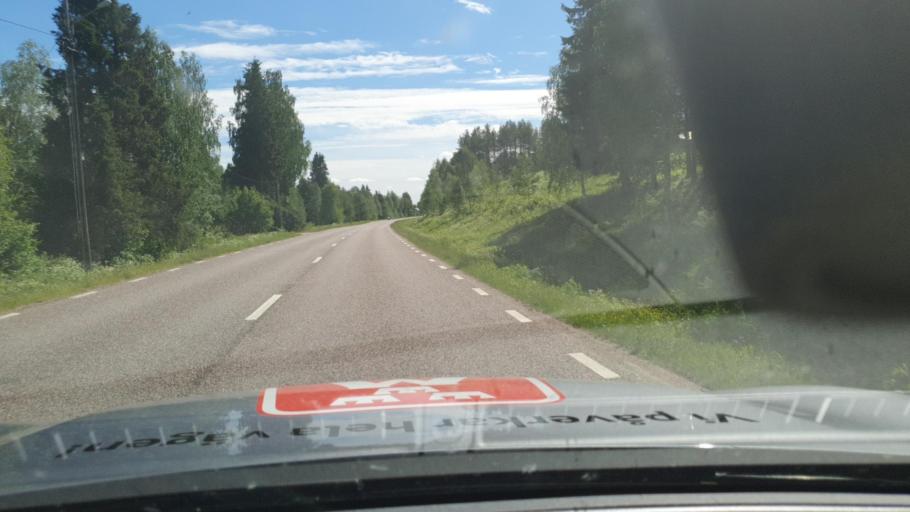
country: FI
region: Lapland
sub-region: Torniolaakso
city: Pello
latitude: 66.9518
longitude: 23.8460
